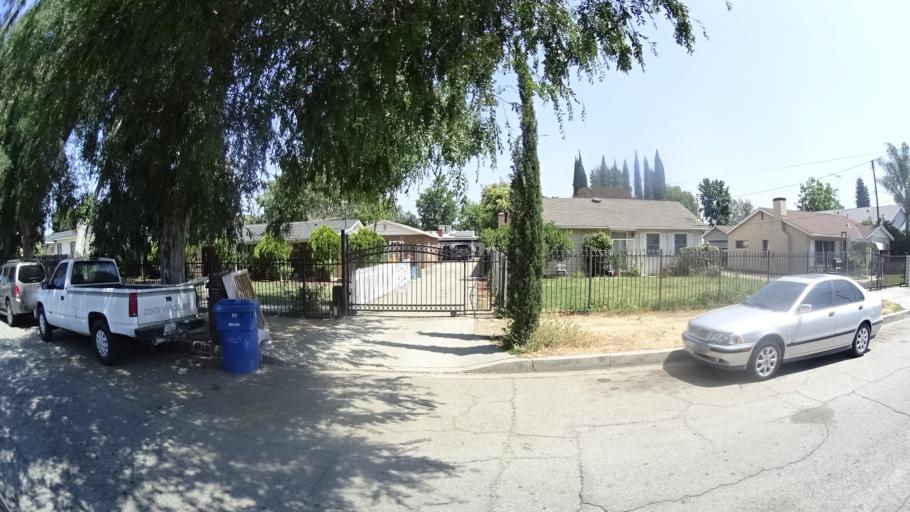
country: US
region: California
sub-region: Los Angeles County
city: Van Nuys
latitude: 34.2031
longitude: -118.4561
